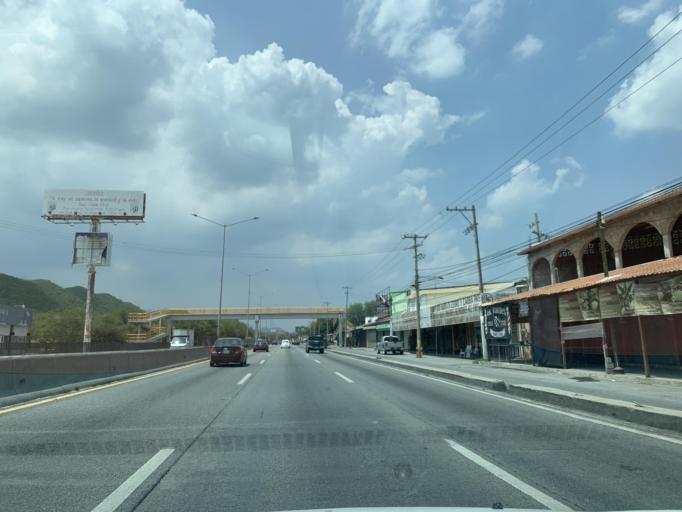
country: MX
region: Nuevo Leon
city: Santiago
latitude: 25.4539
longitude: -100.1646
